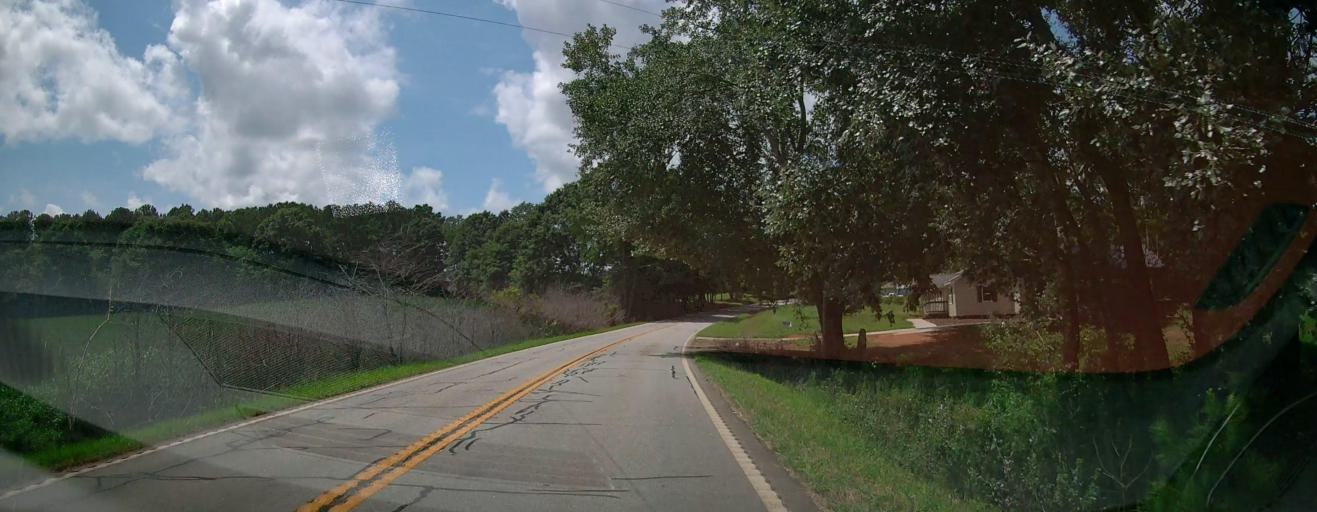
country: US
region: Georgia
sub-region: Carroll County
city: Bowdon
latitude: 33.4183
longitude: -85.2647
